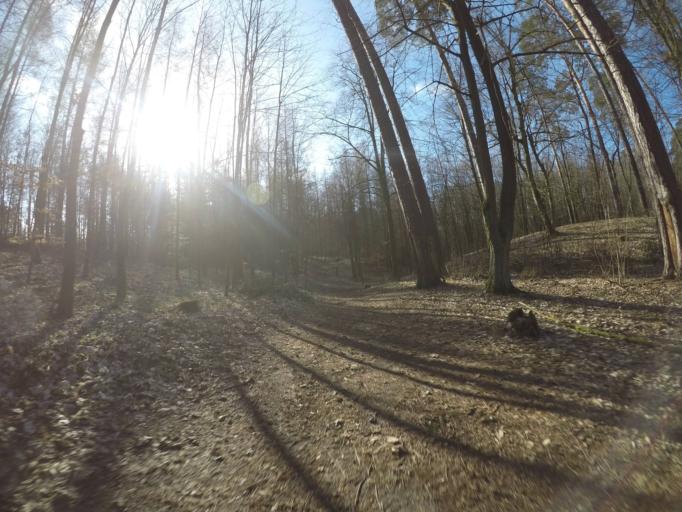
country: PL
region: Kujawsko-Pomorskie
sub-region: Powiat brodnicki
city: Gorzno
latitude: 53.1908
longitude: 19.6586
